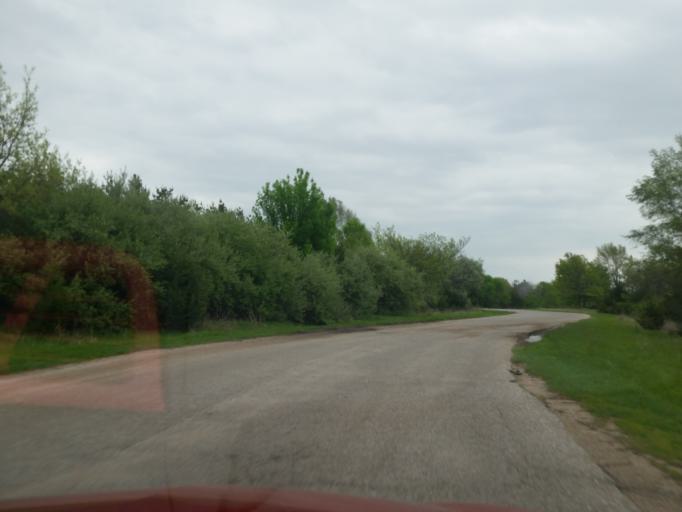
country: US
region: Nebraska
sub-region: Douglas County
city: Bennington
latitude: 41.3190
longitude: -96.1254
